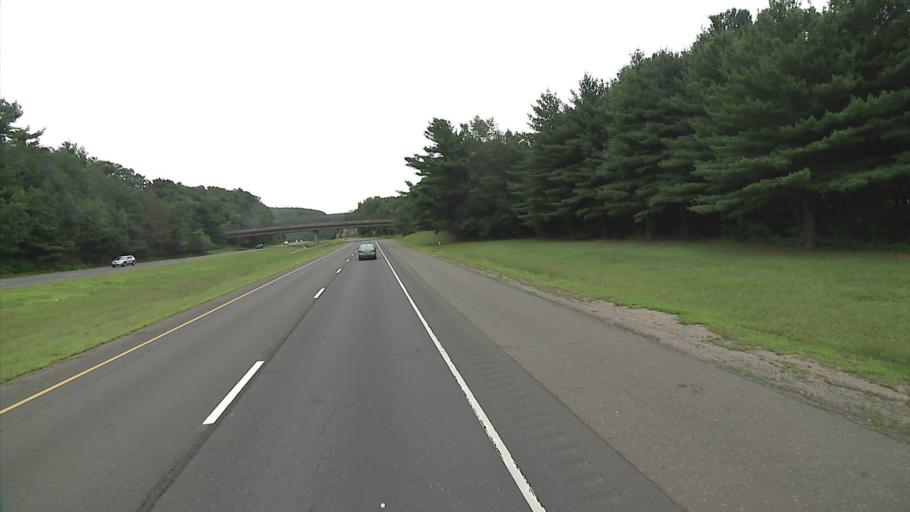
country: US
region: Connecticut
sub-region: New Haven County
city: Seymour
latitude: 41.4378
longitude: -73.0671
